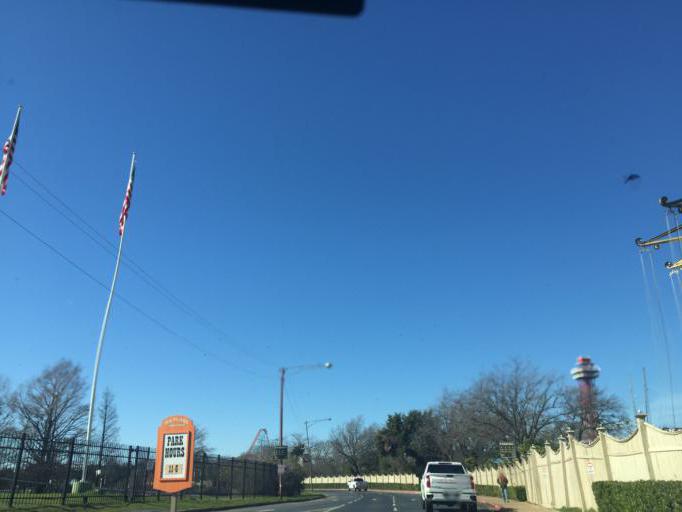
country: US
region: Texas
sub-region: Tarrant County
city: Arlington
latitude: 32.7564
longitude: -97.0664
